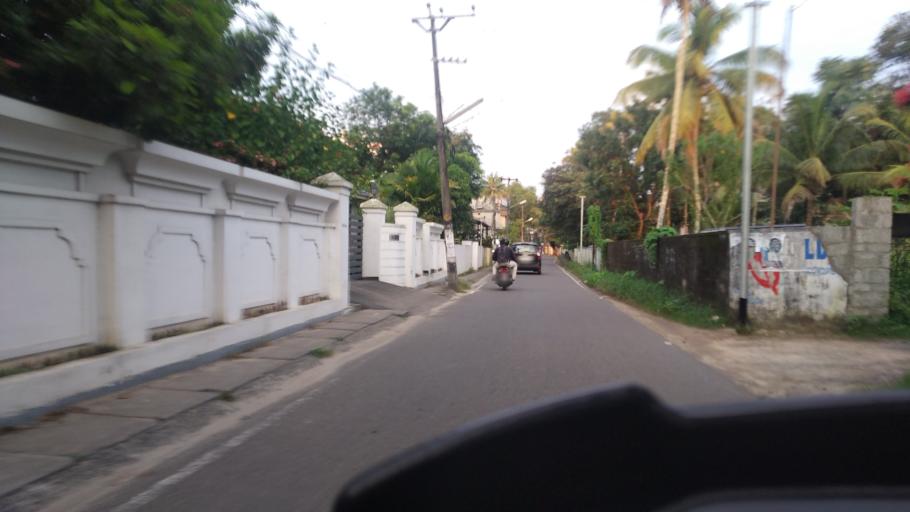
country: IN
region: Kerala
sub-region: Ernakulam
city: Elur
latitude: 10.0306
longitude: 76.2980
